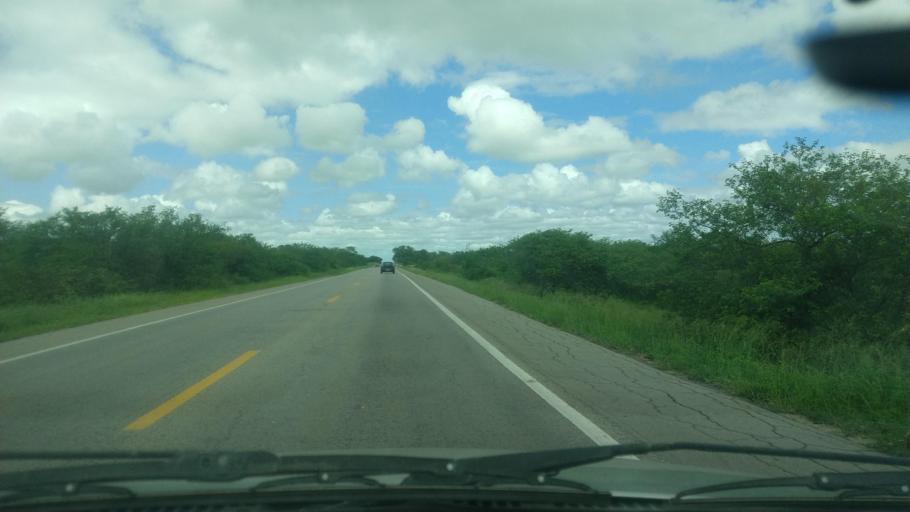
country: BR
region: Rio Grande do Norte
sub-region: Tangara
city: Tangara
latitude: -6.1672
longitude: -35.7589
